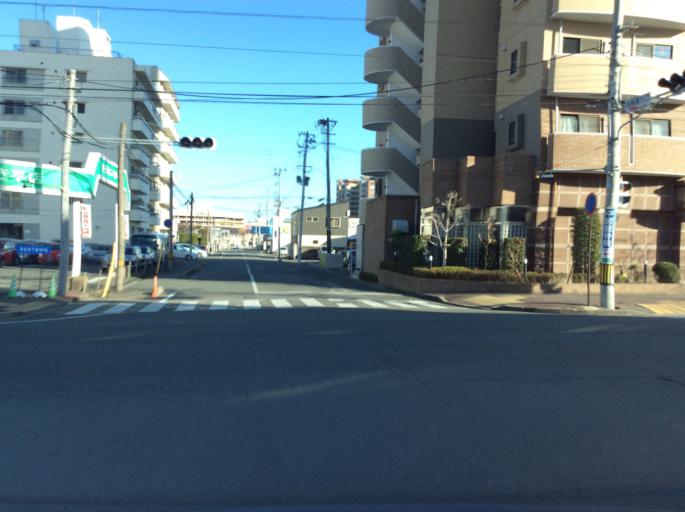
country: JP
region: Fukushima
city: Iwaki
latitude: 37.0509
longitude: 140.8932
